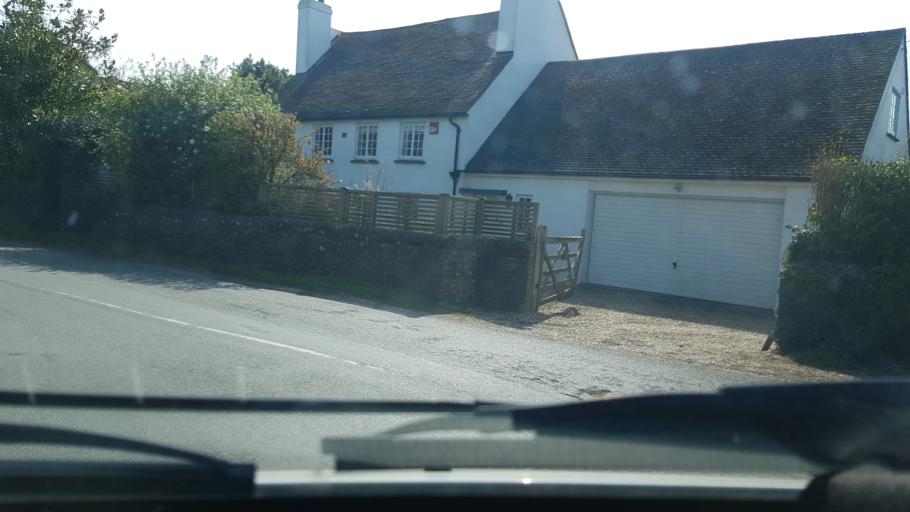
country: GB
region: England
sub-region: West Sussex
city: Chichester
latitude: 50.8180
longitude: -0.8054
